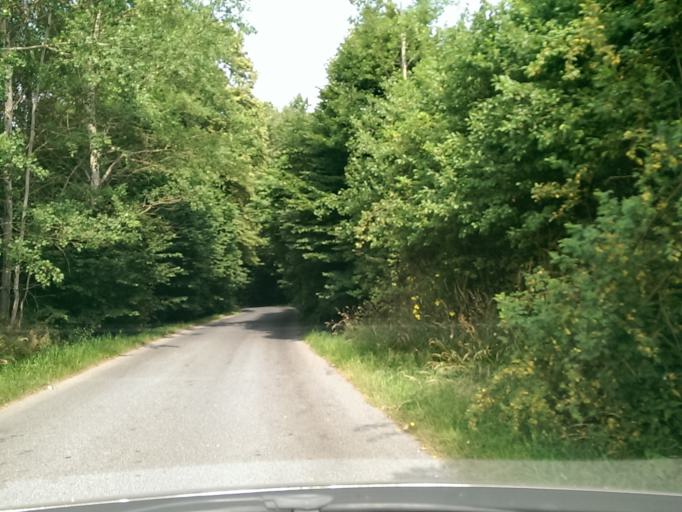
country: CZ
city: Duba
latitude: 50.5385
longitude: 14.5619
